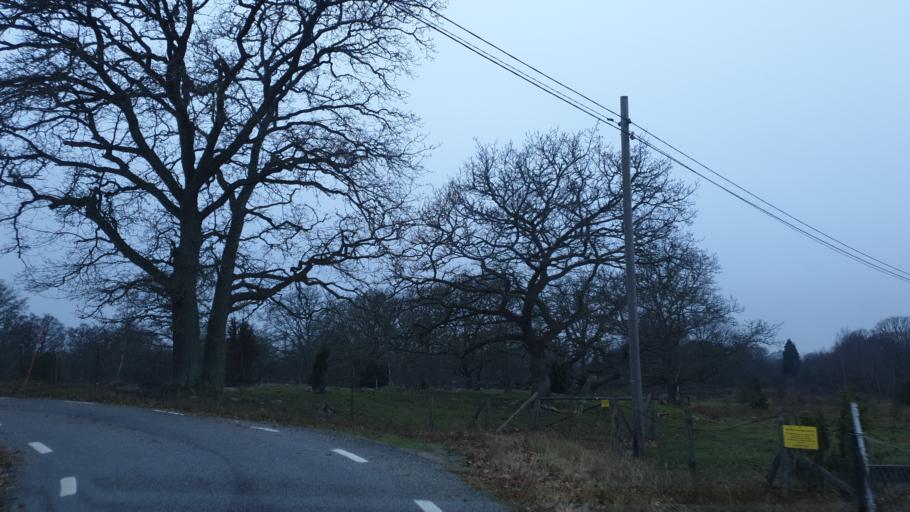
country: SE
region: Blekinge
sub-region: Karlskrona Kommun
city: Karlskrona
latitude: 56.1052
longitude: 15.6063
